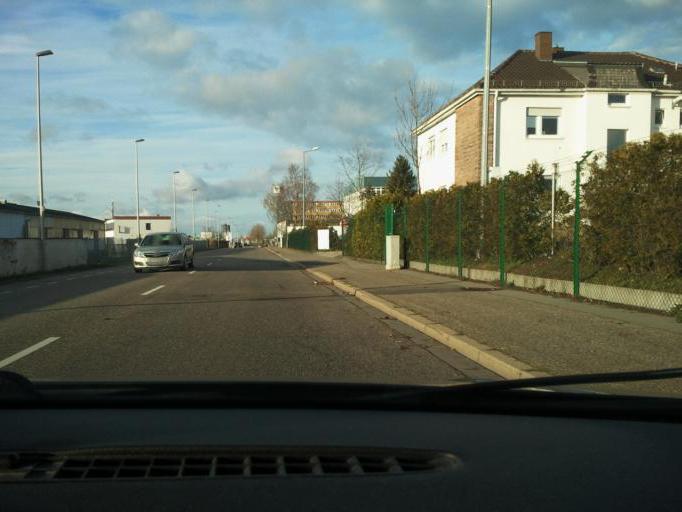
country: DE
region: Rheinland-Pfalz
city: Pirmasens
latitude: 49.2176
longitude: 7.5950
